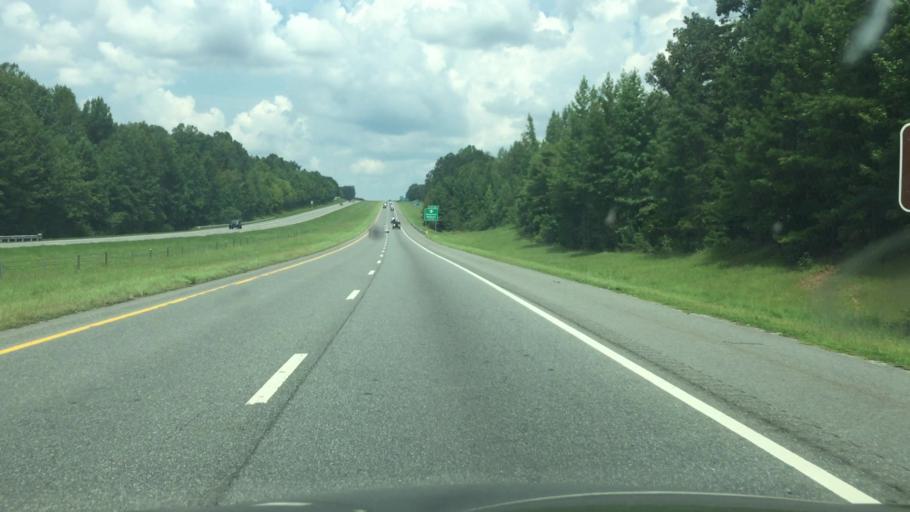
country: US
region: North Carolina
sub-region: Montgomery County
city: Biscoe
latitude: 35.5228
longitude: -79.7838
